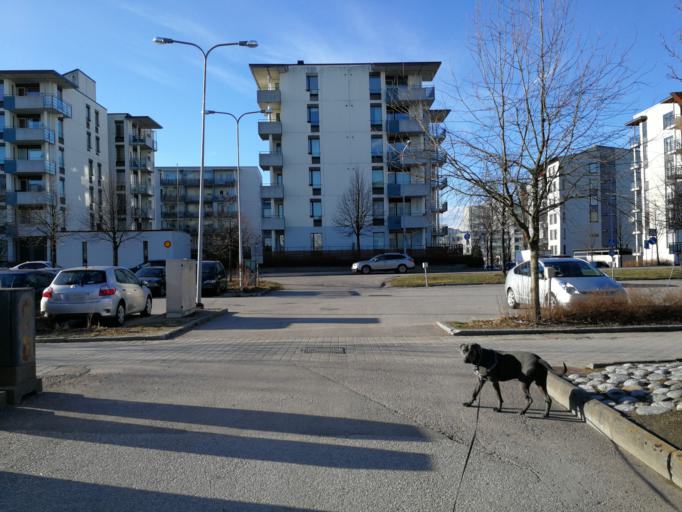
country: FI
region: Uusimaa
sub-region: Helsinki
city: Vantaa
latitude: 60.2052
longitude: 25.1374
